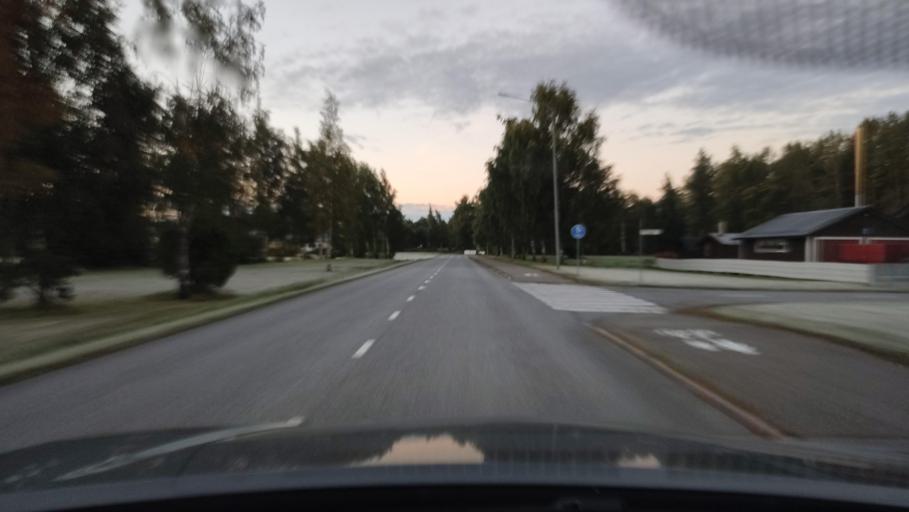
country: FI
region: Ostrobothnia
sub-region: Sydosterbotten
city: Kristinestad
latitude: 62.2773
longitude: 21.3644
